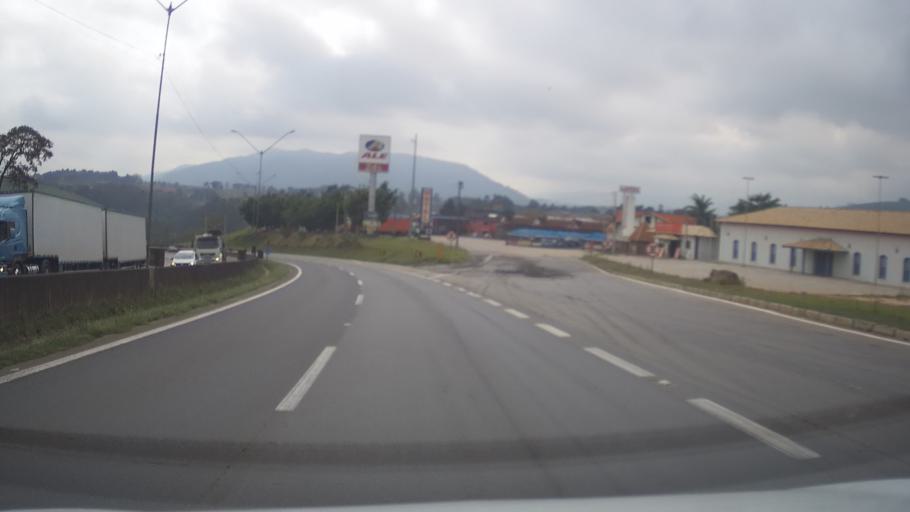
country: BR
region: Minas Gerais
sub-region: Extrema
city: Extrema
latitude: -22.8350
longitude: -46.3207
